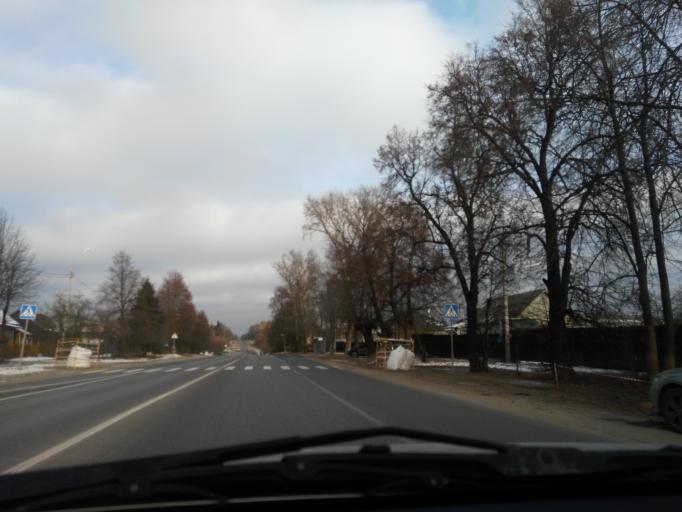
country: RU
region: Moskovskaya
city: Selyatino
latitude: 55.2782
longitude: 37.1153
